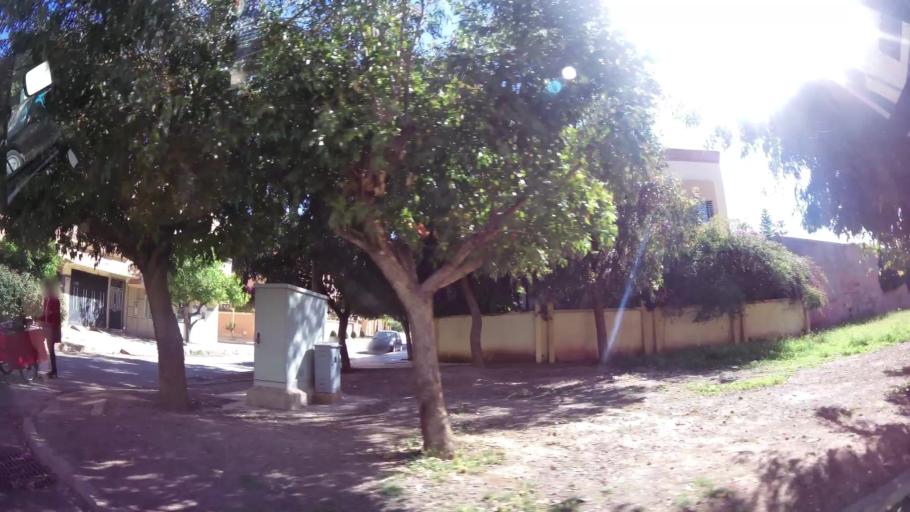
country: MA
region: Oriental
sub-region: Oujda-Angad
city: Oujda
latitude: 34.6572
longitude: -1.8936
